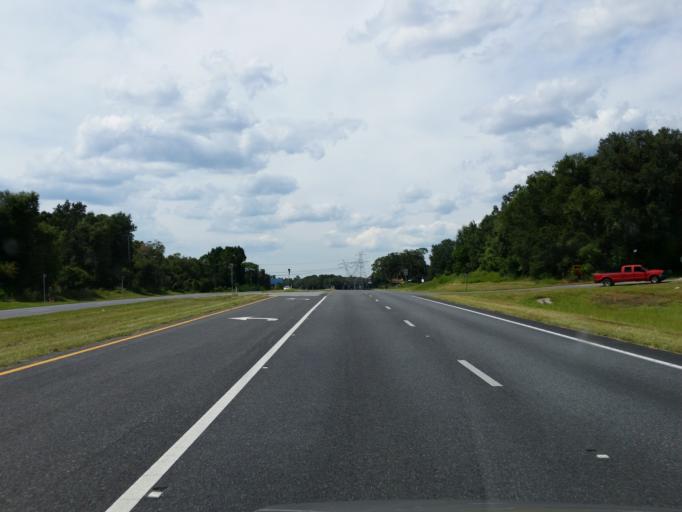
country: US
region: Florida
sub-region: Sumter County
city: Wildwood
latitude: 28.8652
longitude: -82.0783
